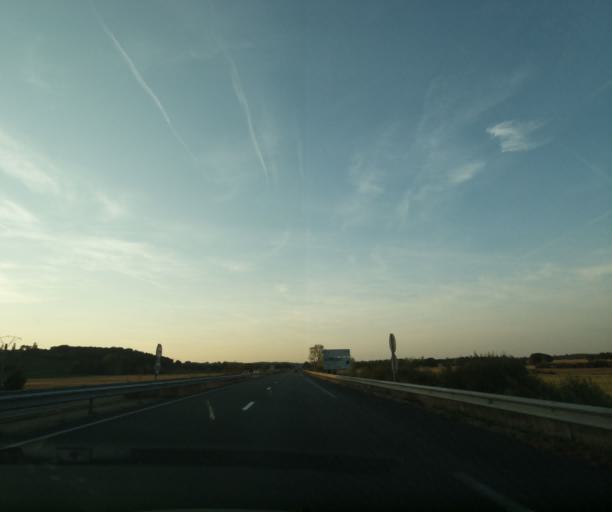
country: FR
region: Aquitaine
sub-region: Departement du Lot-et-Garonne
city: Damazan
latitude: 44.2693
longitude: 0.2775
